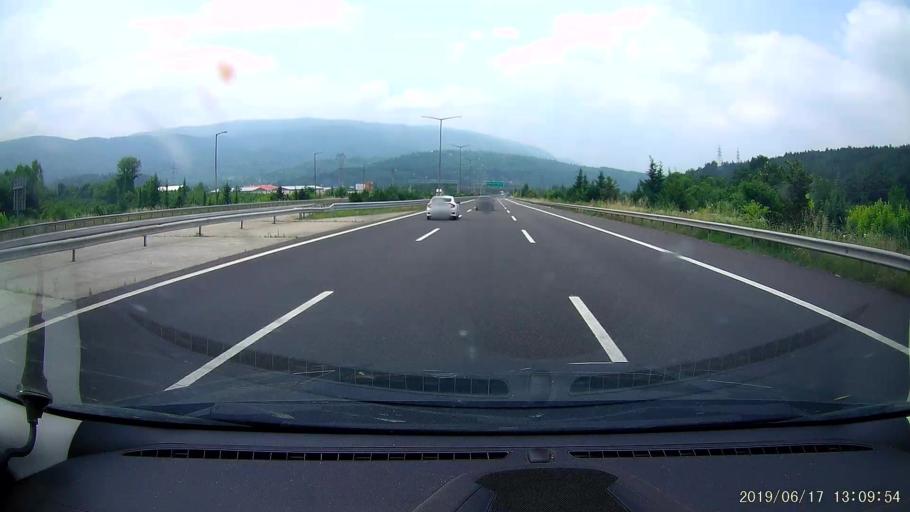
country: TR
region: Duzce
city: Kaynasli
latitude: 40.7898
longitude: 31.2810
